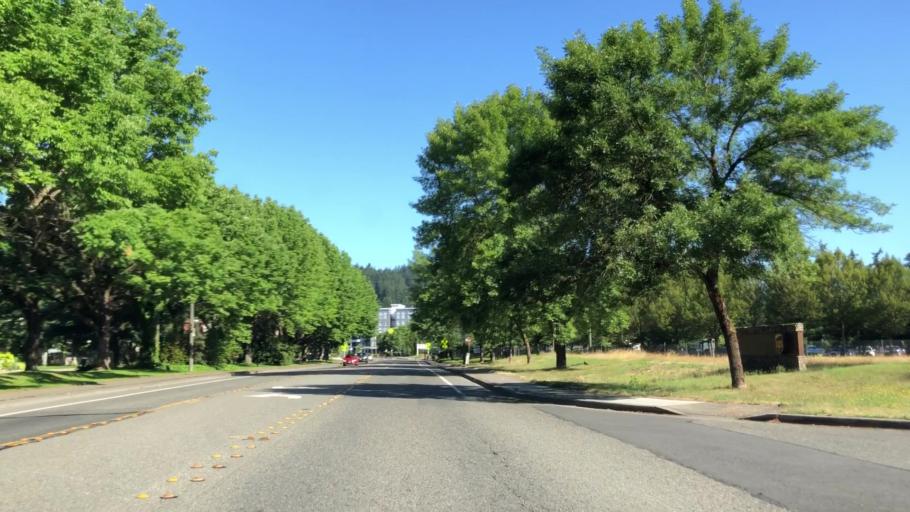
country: US
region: Washington
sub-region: King County
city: Redmond
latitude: 47.6723
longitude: -122.1006
